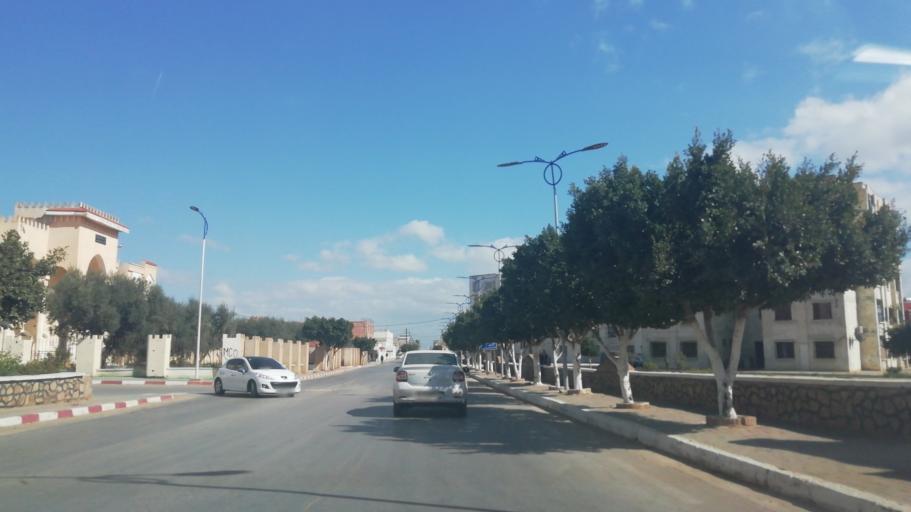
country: DZ
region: Mostaganem
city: Mostaganem
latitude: 35.9998
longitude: 0.3335
